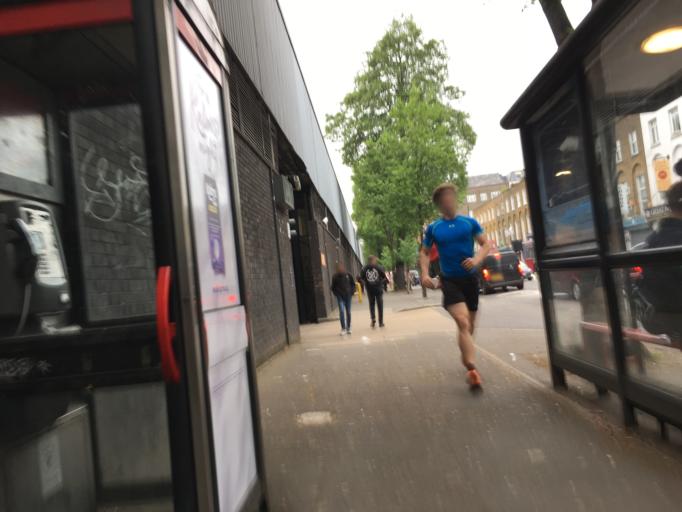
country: GB
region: England
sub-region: Greater London
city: Camden Town
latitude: 51.5289
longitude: -0.1324
